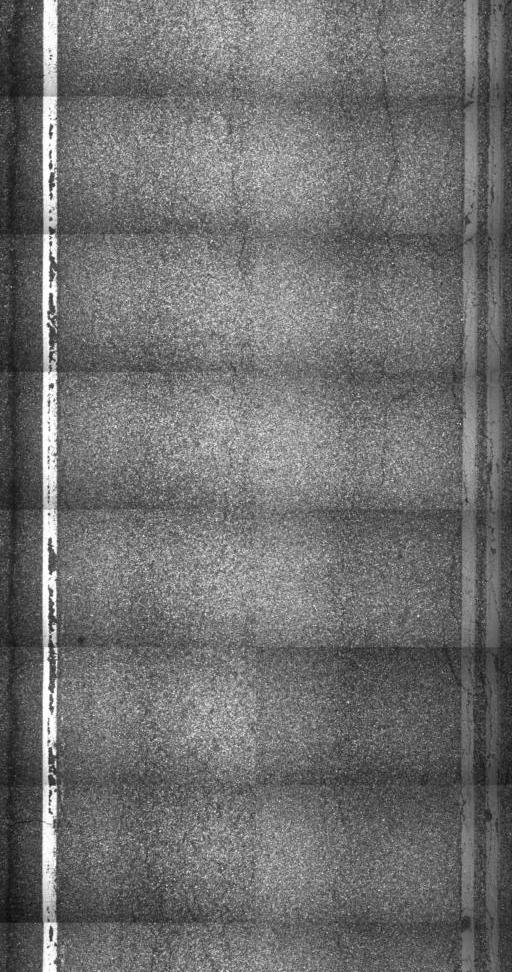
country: US
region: Vermont
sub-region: Rutland County
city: Rutland
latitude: 43.4581
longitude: -72.8862
